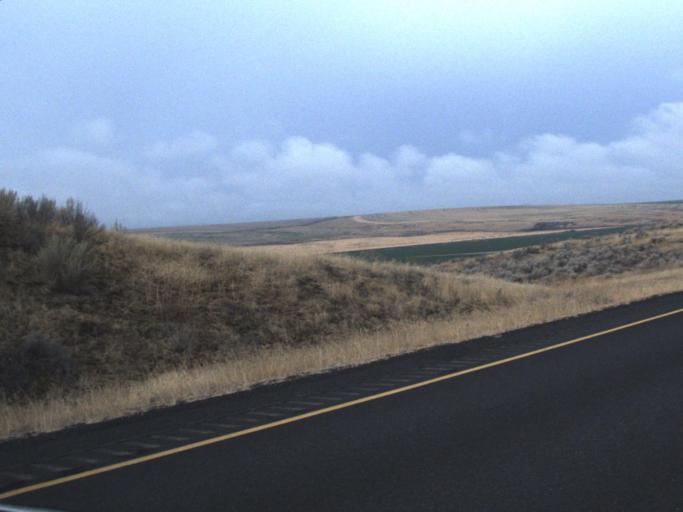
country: US
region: Washington
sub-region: Grant County
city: Warden
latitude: 47.0848
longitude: -118.9607
